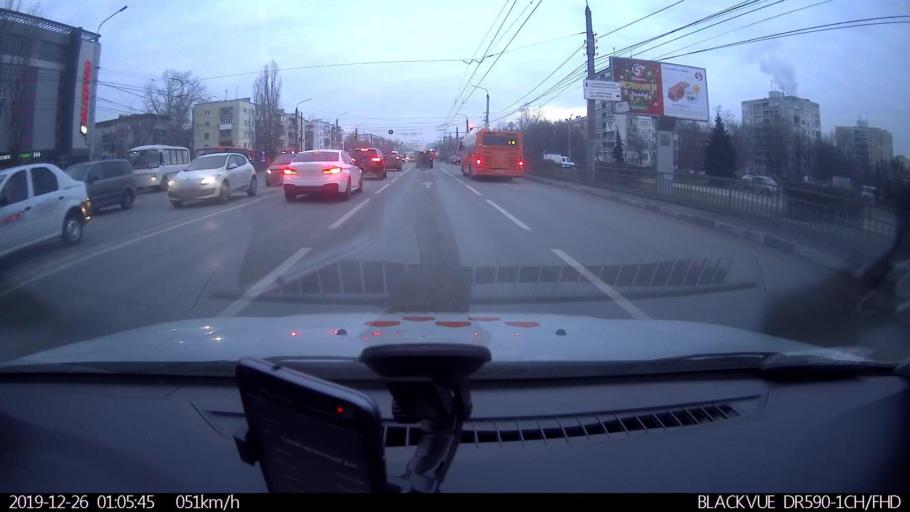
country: RU
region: Nizjnij Novgorod
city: Nizhniy Novgorod
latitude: 56.2869
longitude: 43.9294
